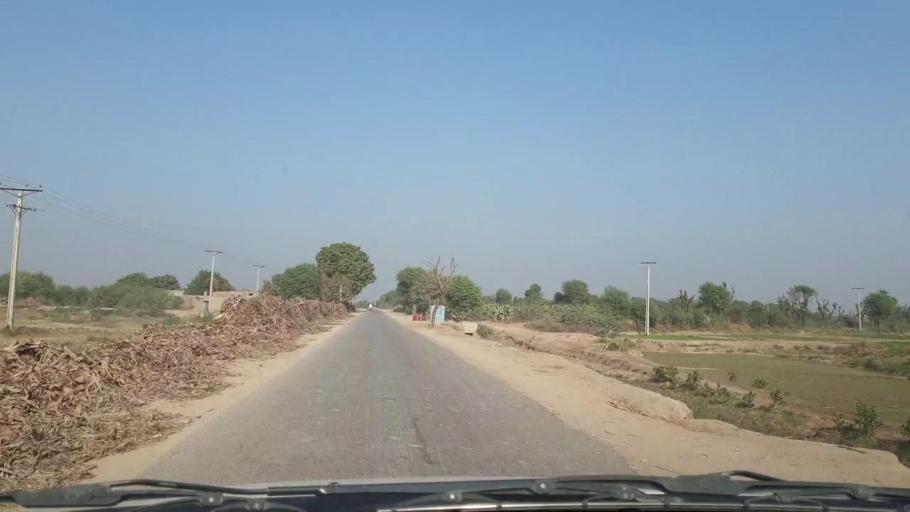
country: PK
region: Sindh
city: Tando Muhammad Khan
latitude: 25.1689
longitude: 68.5887
